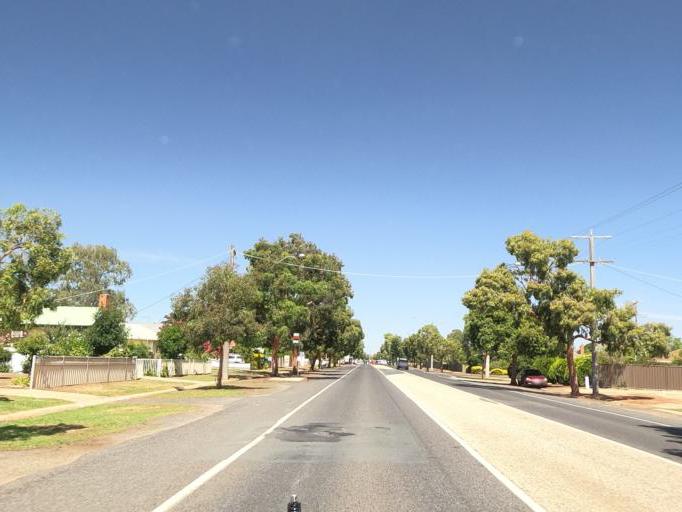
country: AU
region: Victoria
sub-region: Moira
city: Yarrawonga
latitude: -36.0162
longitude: 146.0096
